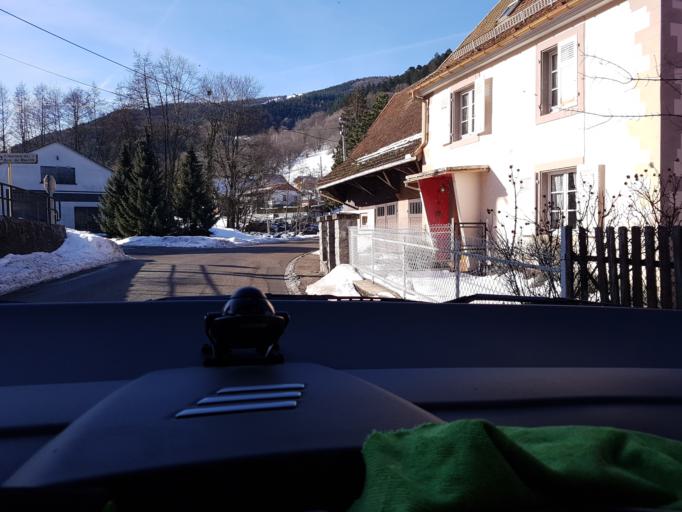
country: FR
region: Alsace
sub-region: Departement du Haut-Rhin
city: Metzeral
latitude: 47.9946
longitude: 7.0724
